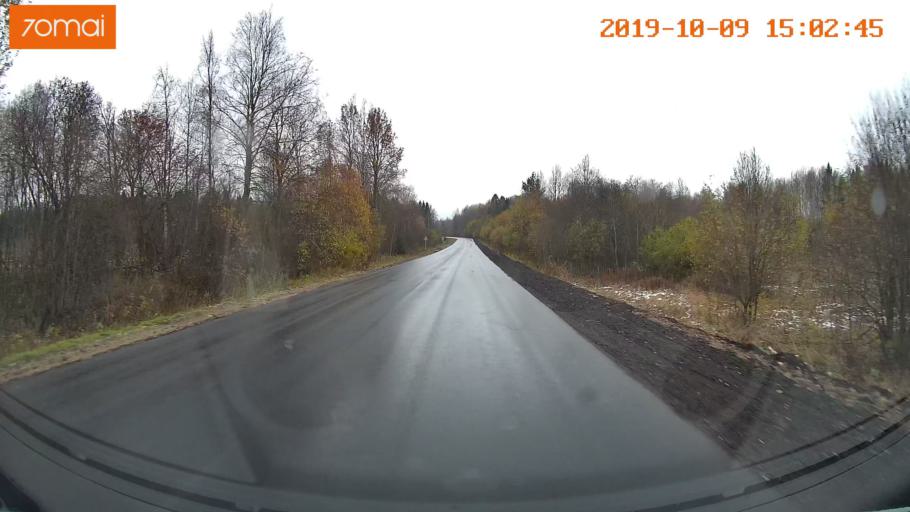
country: RU
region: Kostroma
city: Chistyye Bory
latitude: 58.2805
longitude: 41.6778
